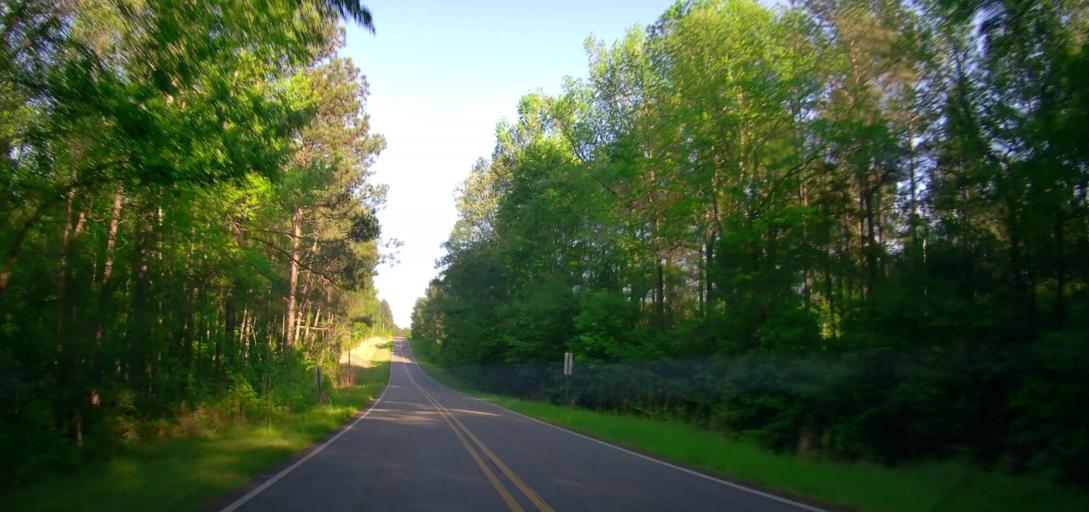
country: US
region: Georgia
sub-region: Putnam County
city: Eatonton
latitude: 33.2848
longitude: -83.3232
